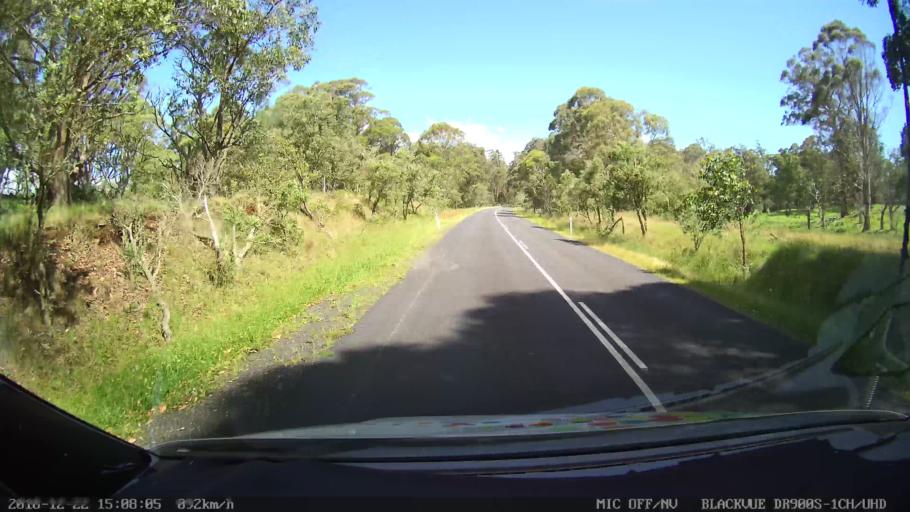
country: AU
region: New South Wales
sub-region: Bellingen
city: Dorrigo
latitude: -30.3077
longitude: 152.4136
